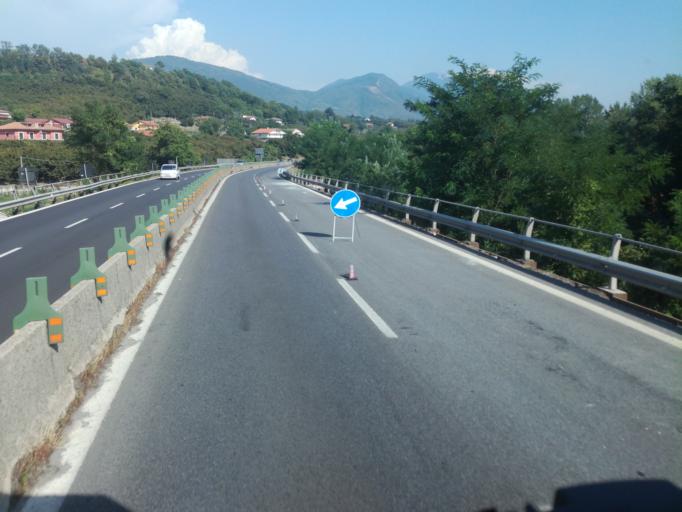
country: IT
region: Campania
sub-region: Provincia di Avellino
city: Atripalda
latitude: 40.9099
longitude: 14.8298
